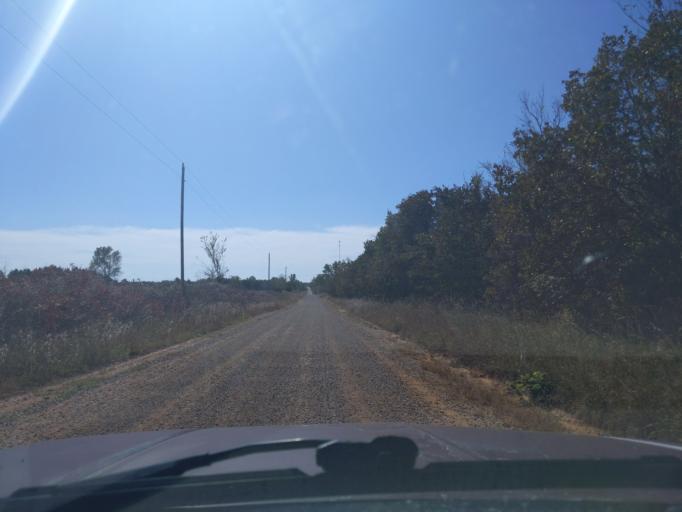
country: US
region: Oklahoma
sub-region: Okfuskee County
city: Boley
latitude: 35.6455
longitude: -96.4235
